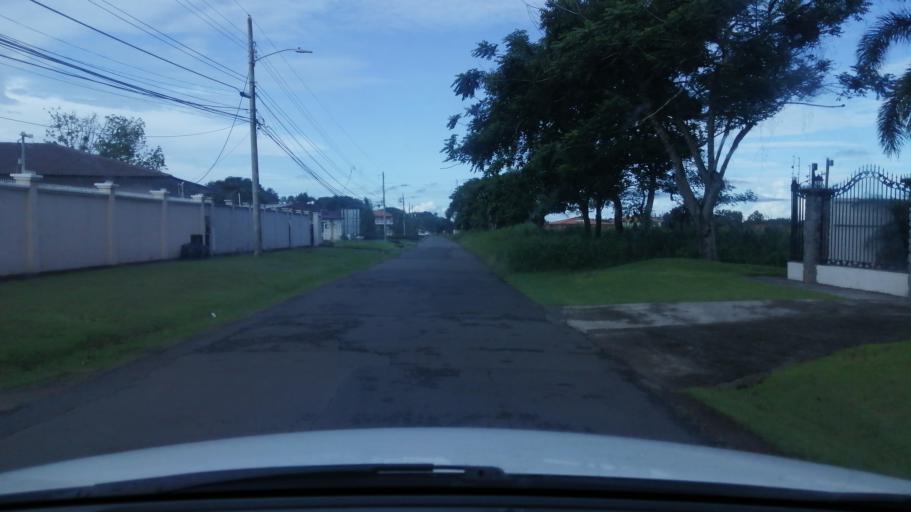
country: PA
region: Chiriqui
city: El Quiteno
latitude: 8.4627
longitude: -82.4165
